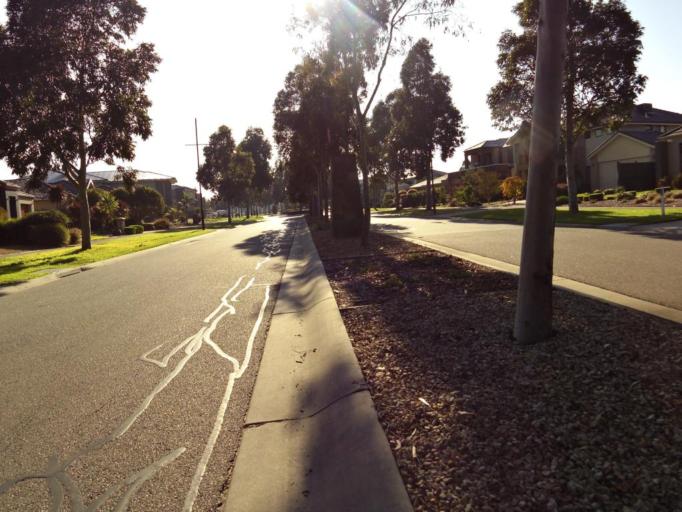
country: AU
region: Victoria
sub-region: Kingston
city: Waterways
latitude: -38.0129
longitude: 145.1317
